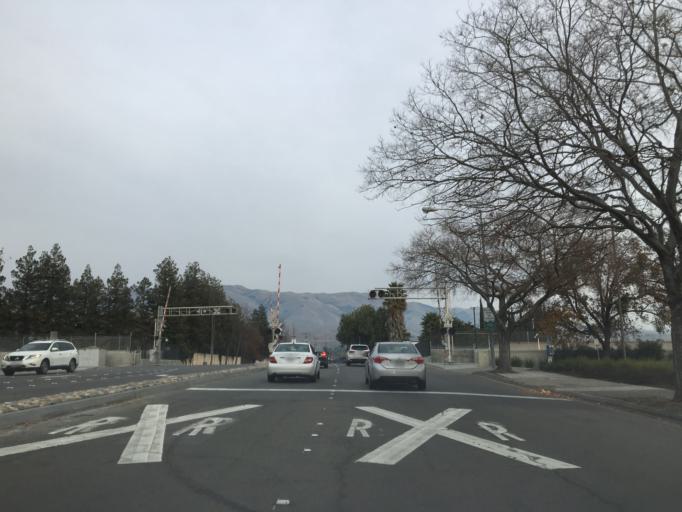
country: US
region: California
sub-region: Santa Clara County
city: Milpitas
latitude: 37.4556
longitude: -121.9167
